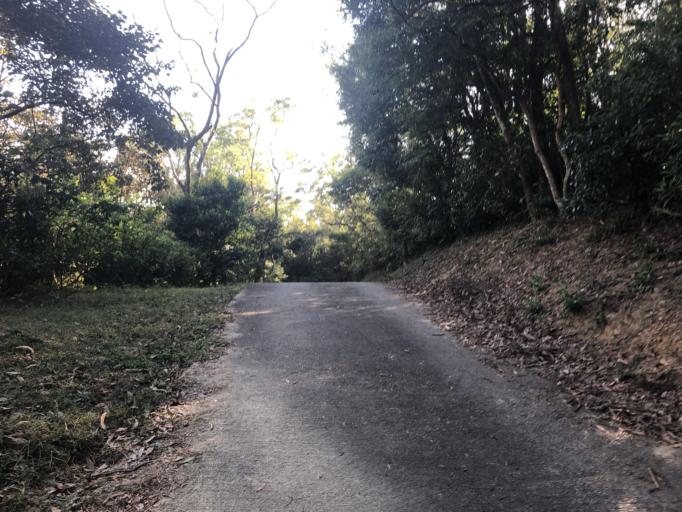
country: HK
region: Tsuen Wan
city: Tsuen Wan
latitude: 22.3906
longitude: 114.0852
